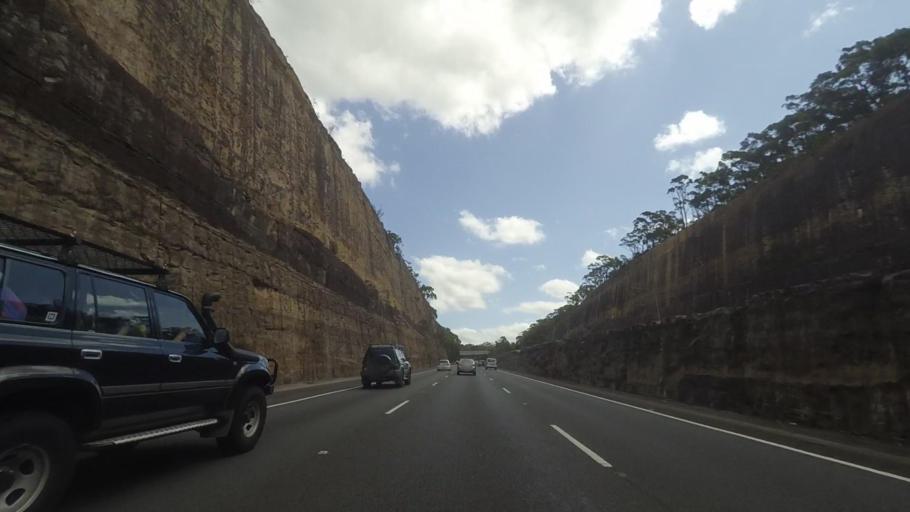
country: AU
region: New South Wales
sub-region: Hornsby Shire
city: Berowra
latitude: -33.6033
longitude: 151.1667
